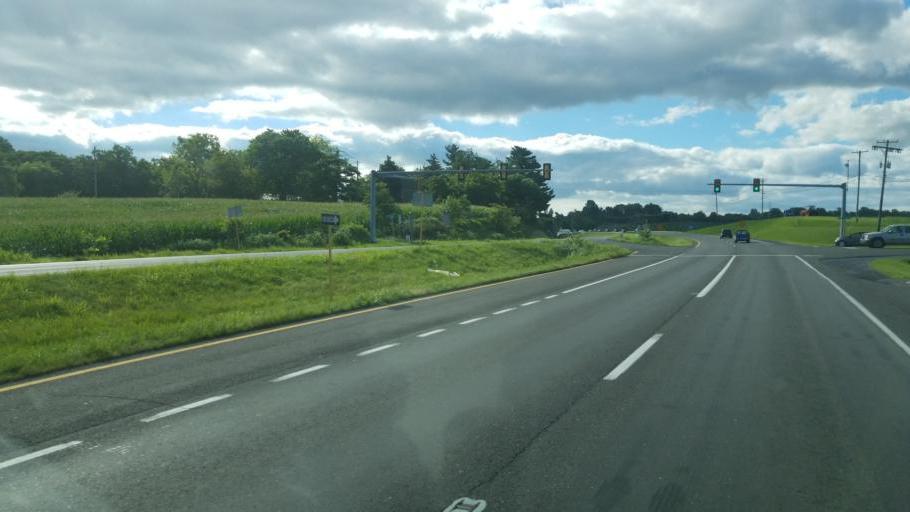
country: US
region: Virginia
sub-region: City of Winchester
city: Winchester
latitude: 39.2154
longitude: -78.1915
